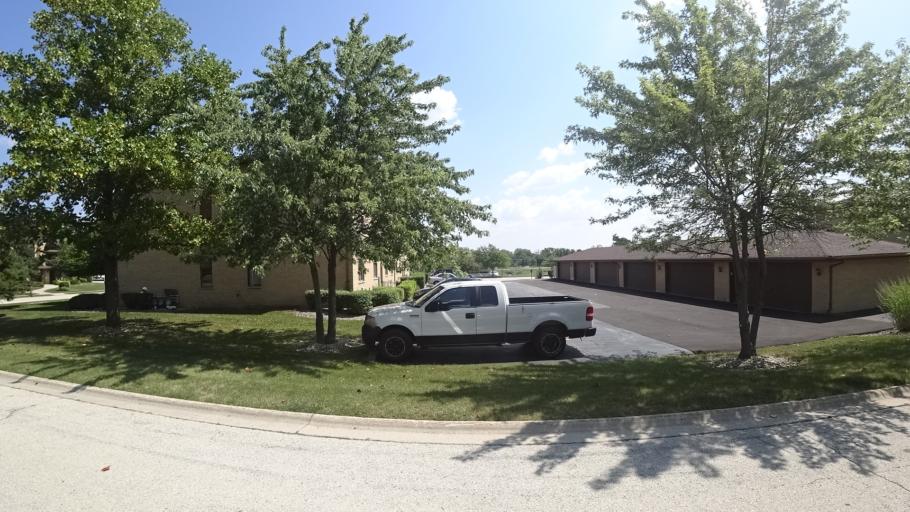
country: US
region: Illinois
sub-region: Cook County
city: Tinley Park
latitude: 41.6159
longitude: -87.7977
